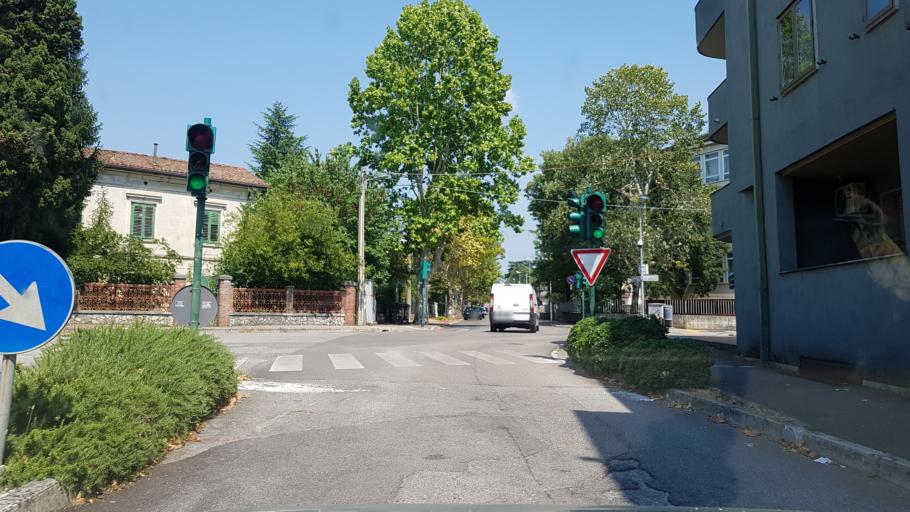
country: IT
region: Friuli Venezia Giulia
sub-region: Provincia di Gorizia
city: Gradisca d'Isonzo
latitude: 45.8901
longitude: 13.4954
